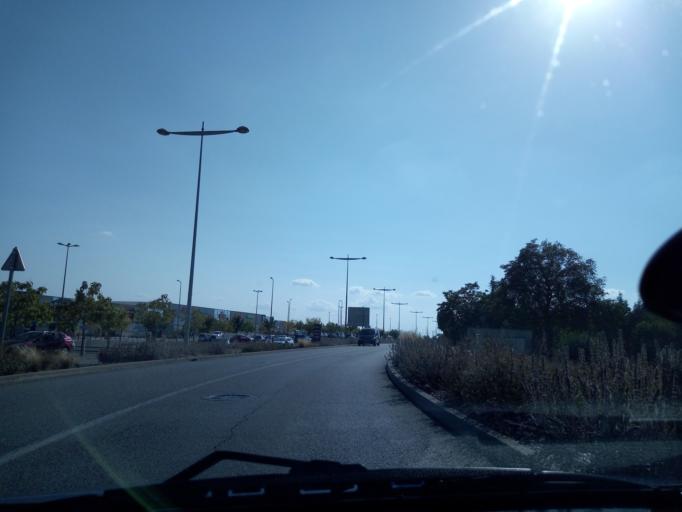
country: FR
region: Midi-Pyrenees
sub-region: Departement de l'Aveyron
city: Sebazac-Concoures
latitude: 44.3984
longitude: 2.6071
